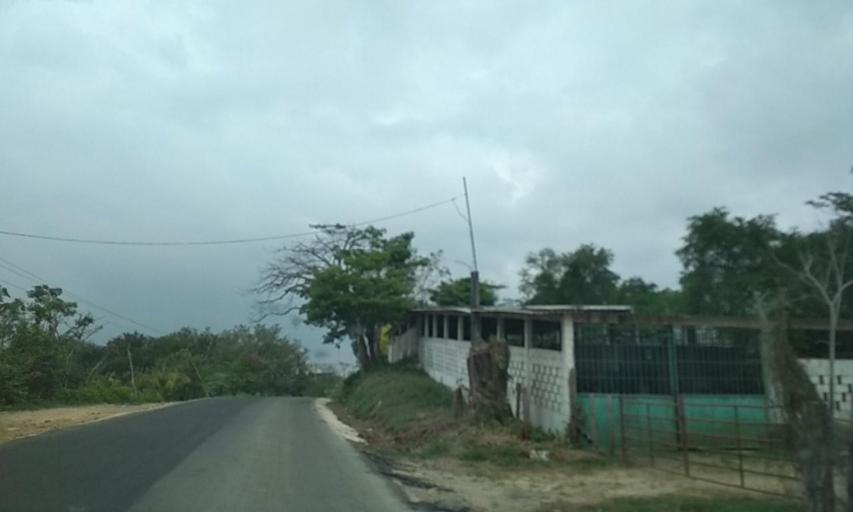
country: MX
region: Tabasco
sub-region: Huimanguillo
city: Francisco Rueda
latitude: 17.7262
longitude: -94.1011
